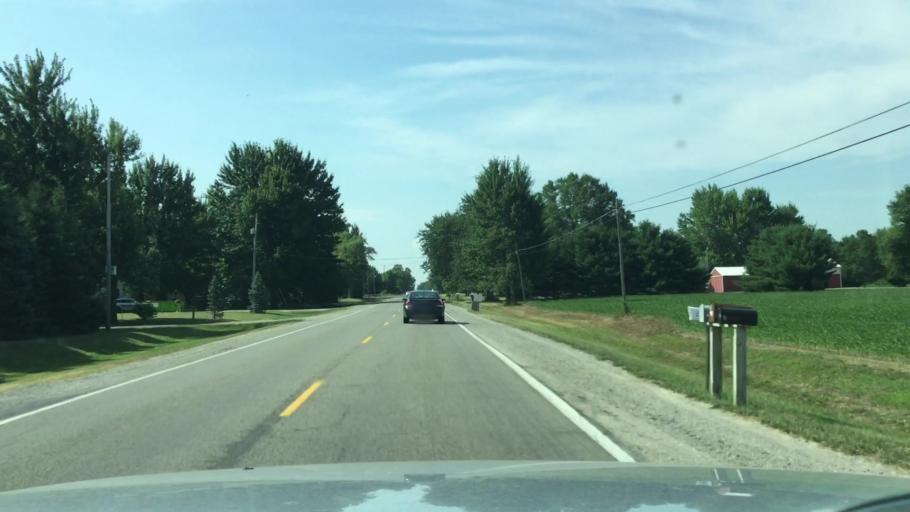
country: US
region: Michigan
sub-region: Genesee County
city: Flushing
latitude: 43.1072
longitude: -83.8137
